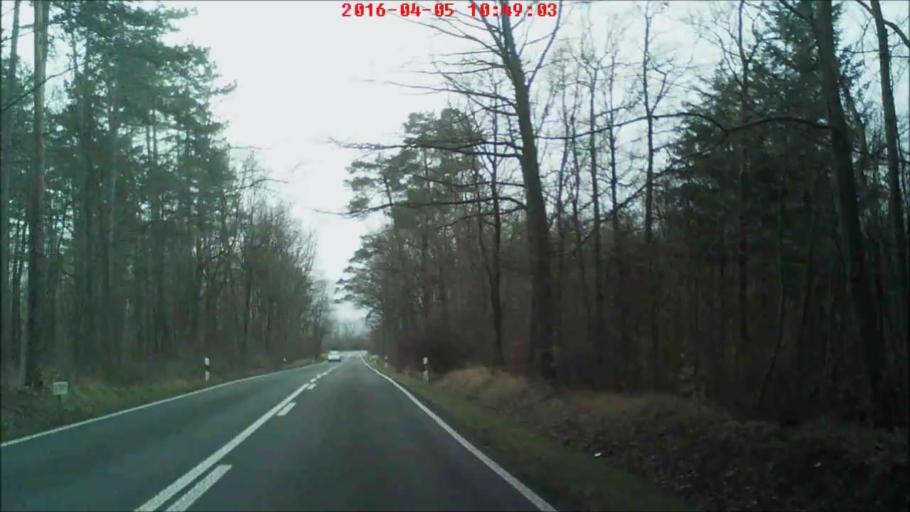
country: DE
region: Thuringia
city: Trochtelborn
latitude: 51.0229
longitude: 10.8195
